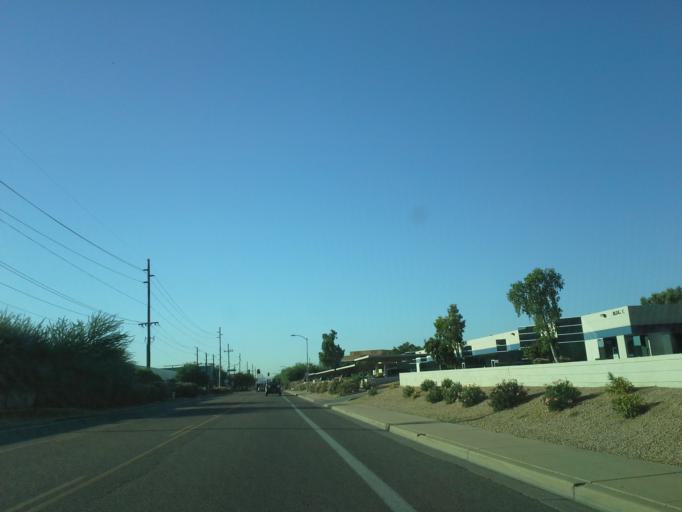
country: US
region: Arizona
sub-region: Maricopa County
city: Glendale
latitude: 33.5841
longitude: -112.1082
